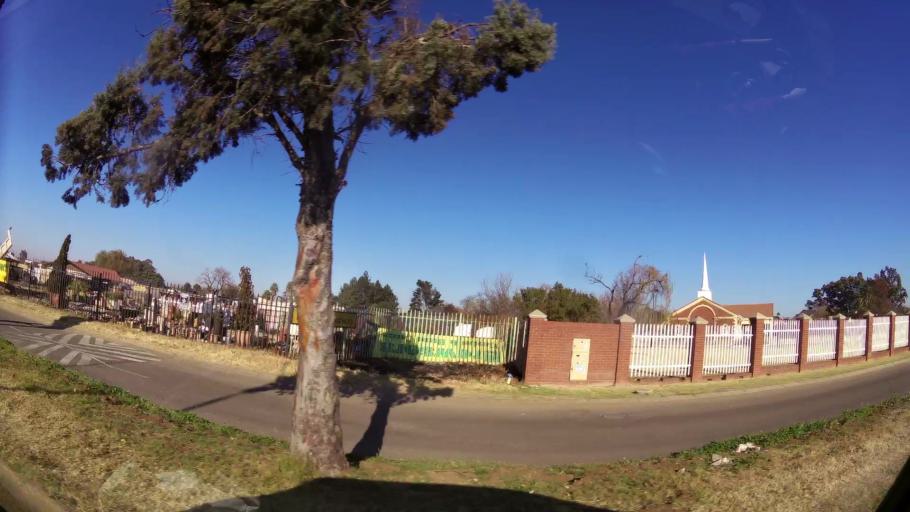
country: ZA
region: Gauteng
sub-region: Ekurhuleni Metropolitan Municipality
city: Germiston
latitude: -26.2852
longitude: 28.1319
